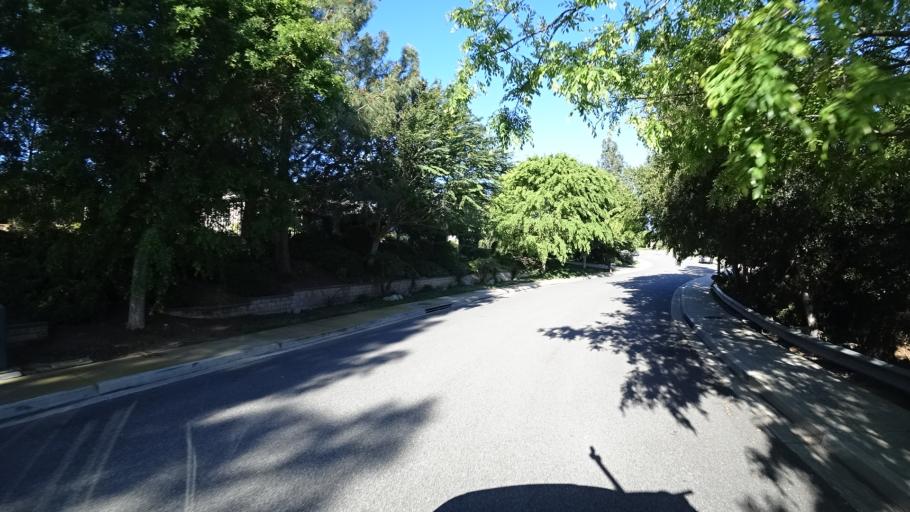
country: US
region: California
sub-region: Ventura County
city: Casa Conejo
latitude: 34.1852
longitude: -118.9008
